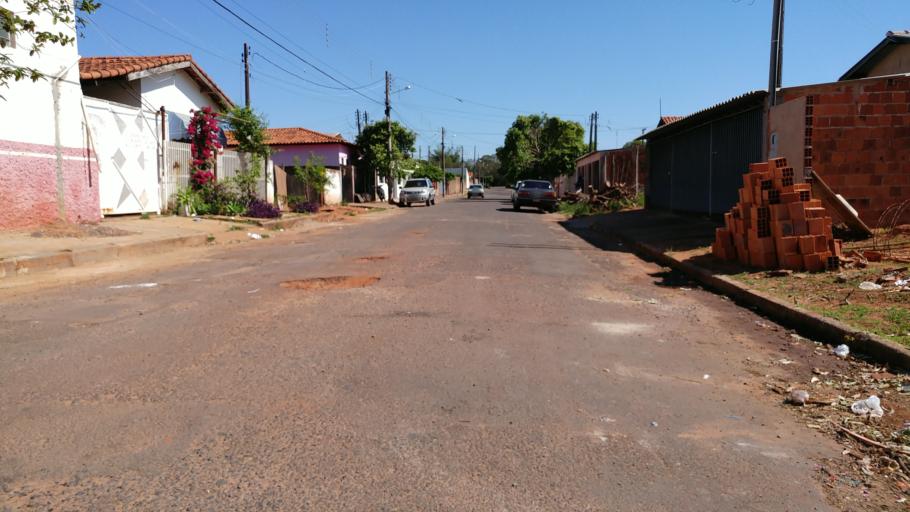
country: BR
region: Sao Paulo
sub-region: Paraguacu Paulista
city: Paraguacu Paulista
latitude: -22.4277
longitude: -50.5862
